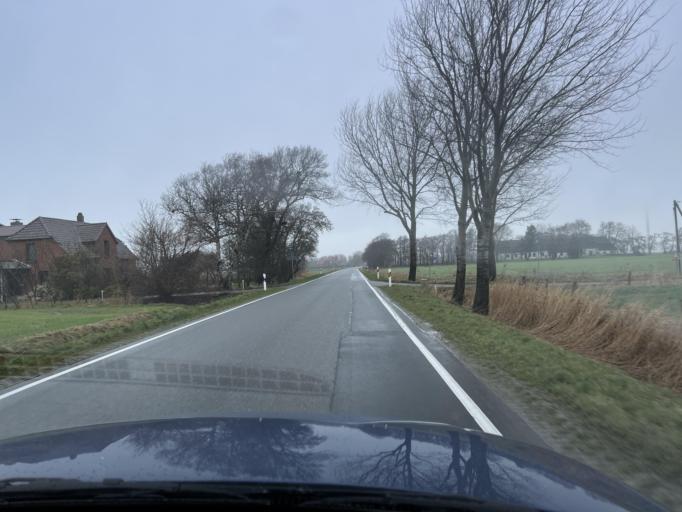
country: DE
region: Schleswig-Holstein
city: Neuenkirchen
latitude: 54.2398
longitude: 9.0019
